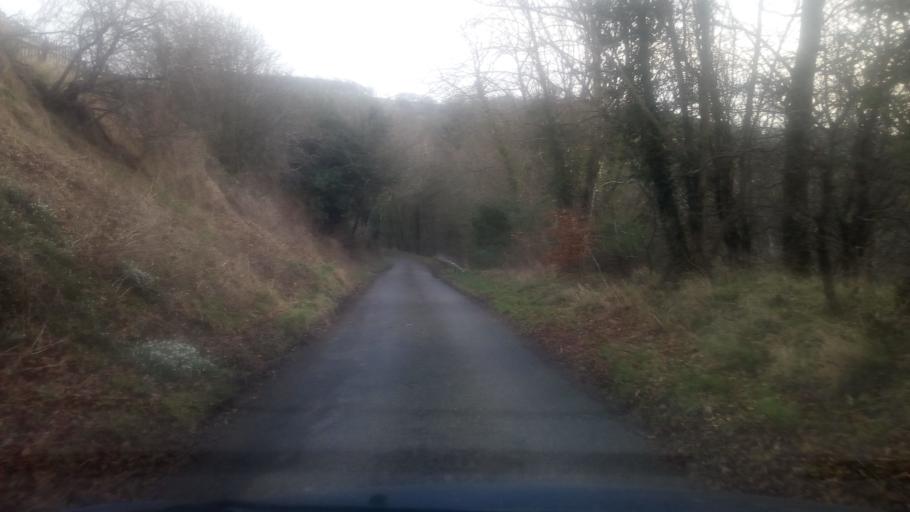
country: GB
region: Scotland
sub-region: The Scottish Borders
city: Jedburgh
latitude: 55.4631
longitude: -2.5558
